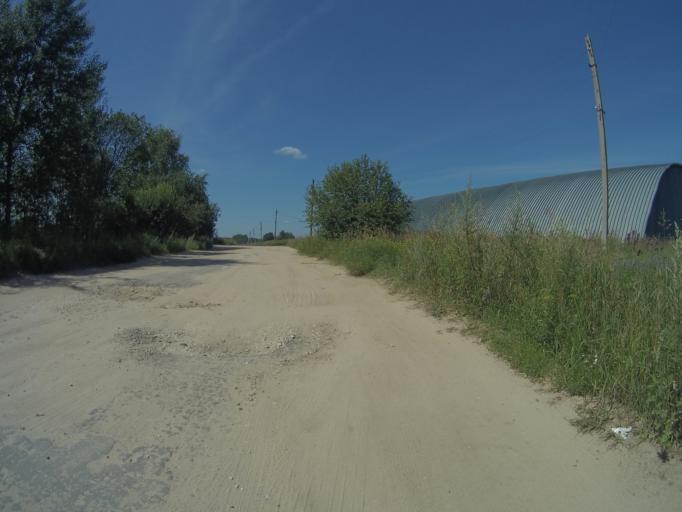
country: RU
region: Vladimir
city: Raduzhnyy
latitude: 56.0267
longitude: 40.3083
